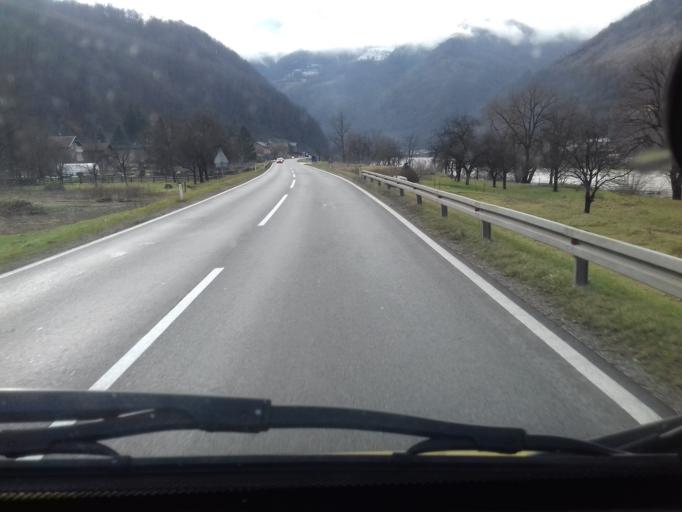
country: BA
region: Federation of Bosnia and Herzegovina
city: Zeljezno Polje
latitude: 44.3251
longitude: 17.9106
